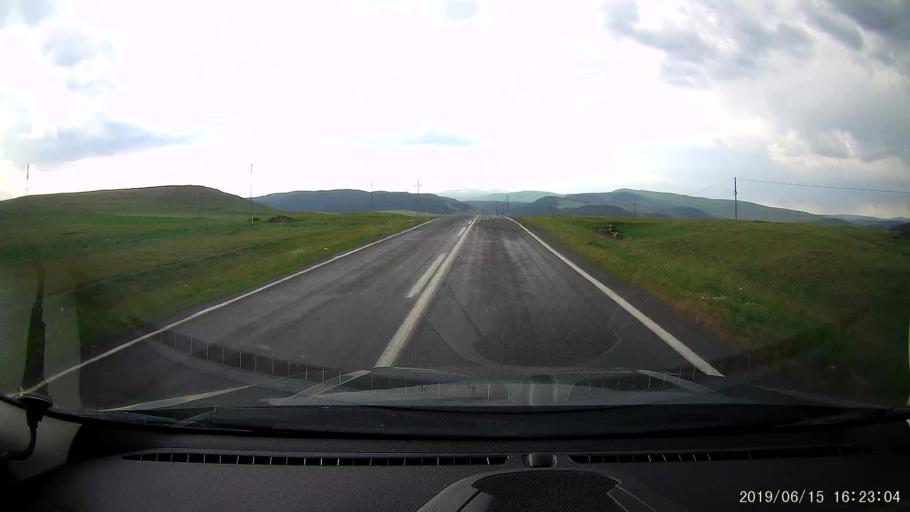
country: TR
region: Ardahan
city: Hanak
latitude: 41.1811
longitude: 42.8575
